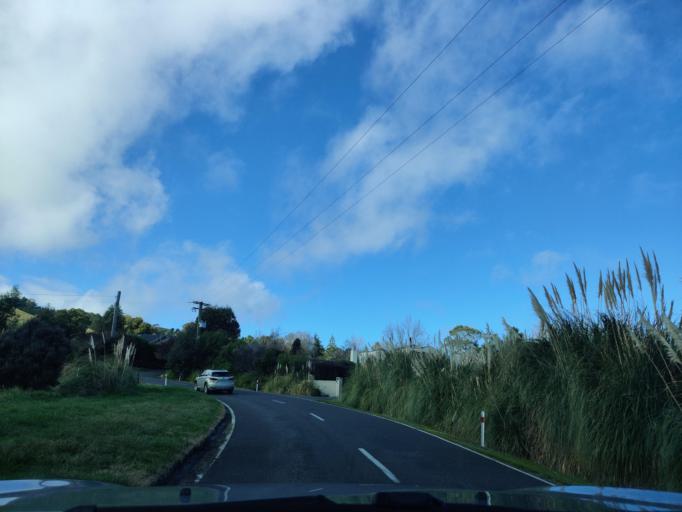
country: NZ
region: Hawke's Bay
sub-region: Hastings District
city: Hastings
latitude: -39.6890
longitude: 176.8991
